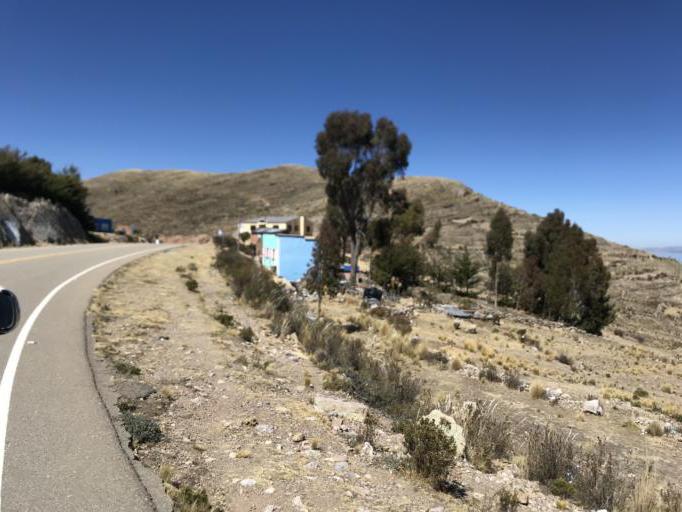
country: BO
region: La Paz
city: San Pedro
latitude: -16.2003
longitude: -68.9035
